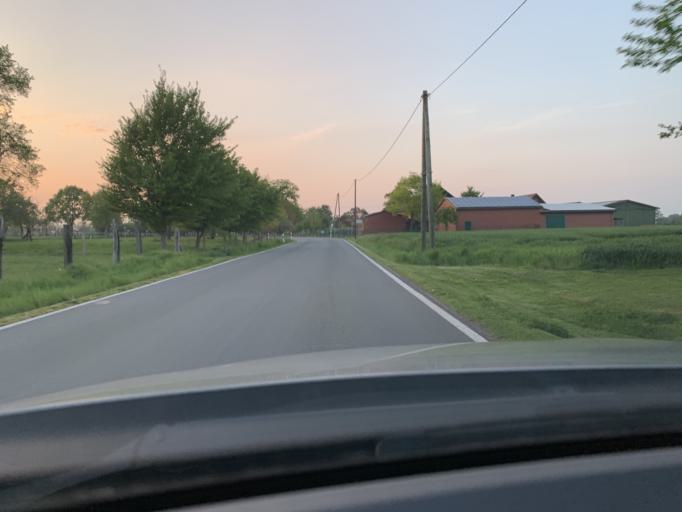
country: DE
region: North Rhine-Westphalia
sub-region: Regierungsbezirk Detmold
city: Langenberg
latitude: 51.7888
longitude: 8.3720
